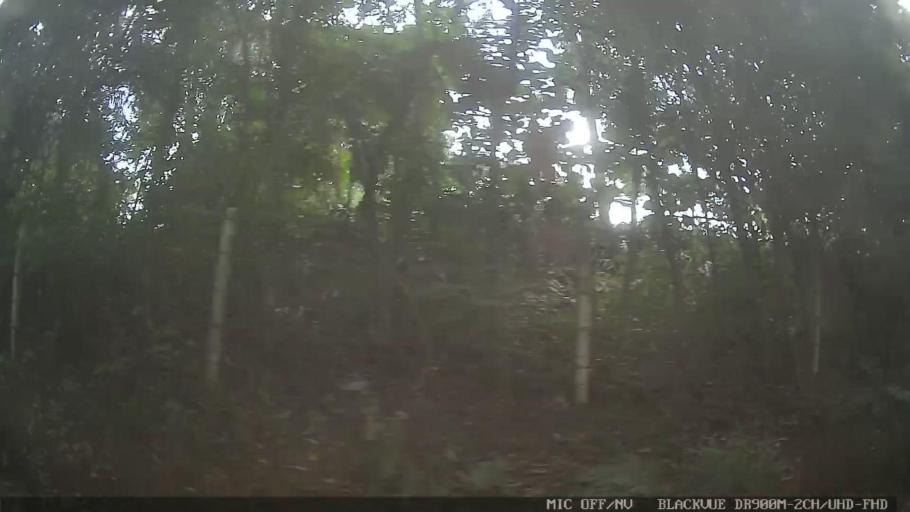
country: BR
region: Sao Paulo
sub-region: Braganca Paulista
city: Braganca Paulista
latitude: -23.0294
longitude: -46.5294
